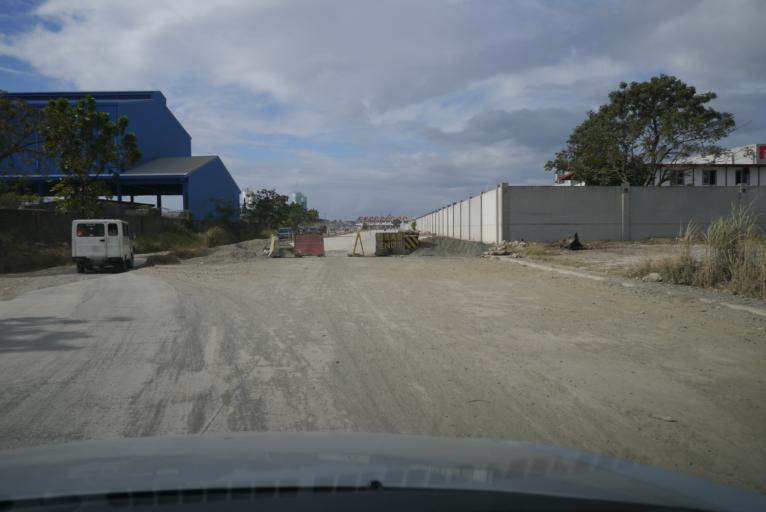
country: PH
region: Calabarzon
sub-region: Province of Rizal
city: Taytay
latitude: 14.5471
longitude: 121.1285
